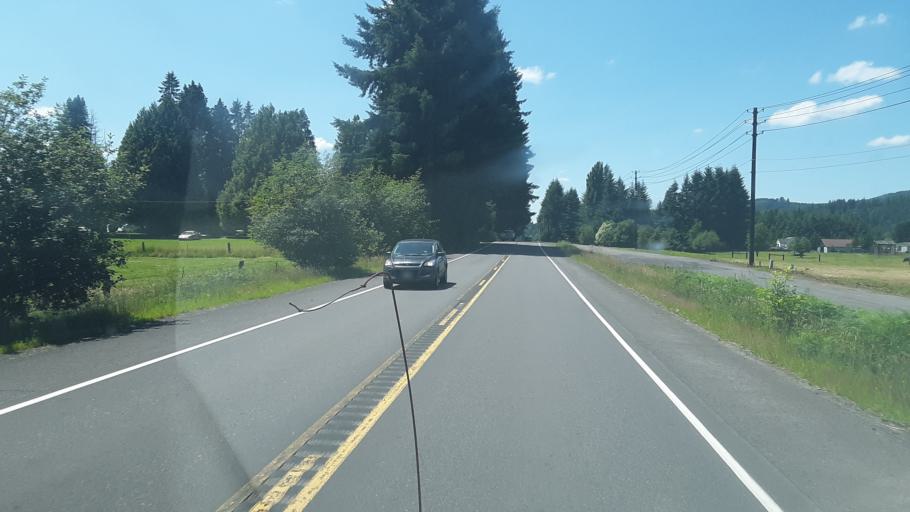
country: US
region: Washington
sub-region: Clark County
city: Amboy
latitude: 45.9243
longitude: -122.4009
